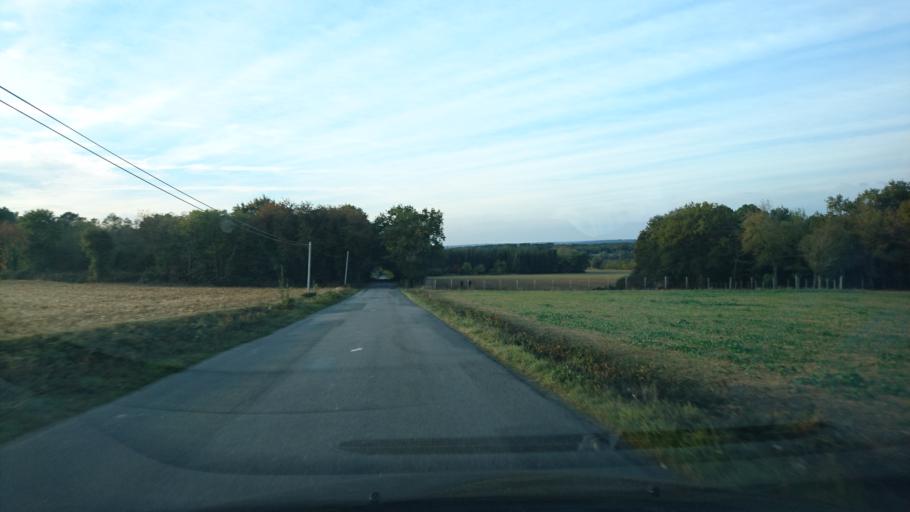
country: FR
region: Brittany
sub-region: Departement d'Ille-et-Vilaine
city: Sixt-sur-Aff
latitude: 47.7641
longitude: -2.0696
